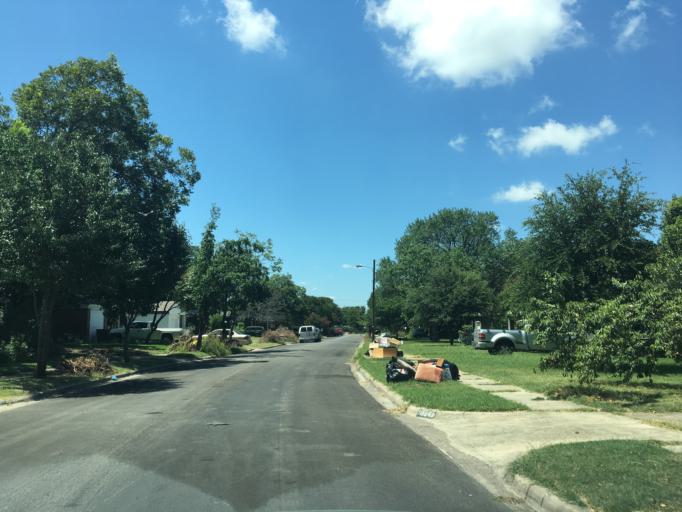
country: US
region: Texas
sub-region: Dallas County
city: Garland
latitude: 32.8407
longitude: -96.6823
